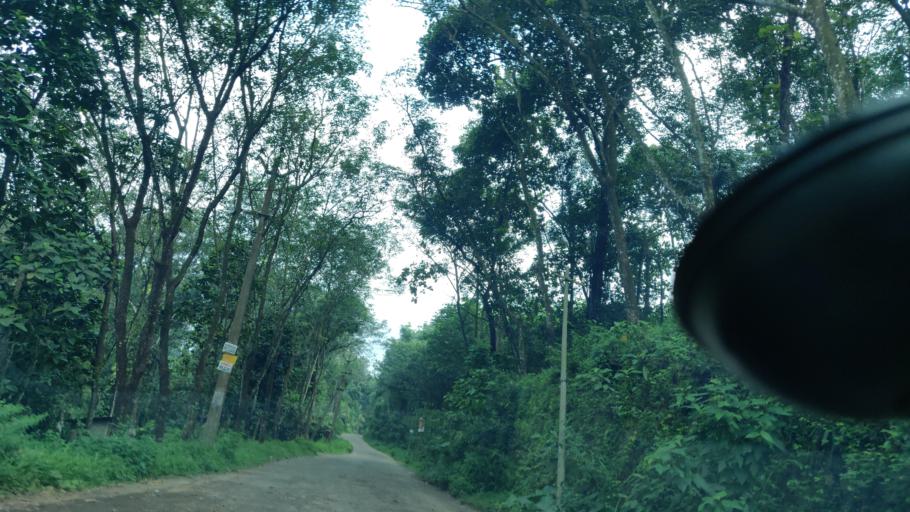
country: IN
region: Kerala
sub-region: Kottayam
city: Palackattumala
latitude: 9.8464
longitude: 76.7034
